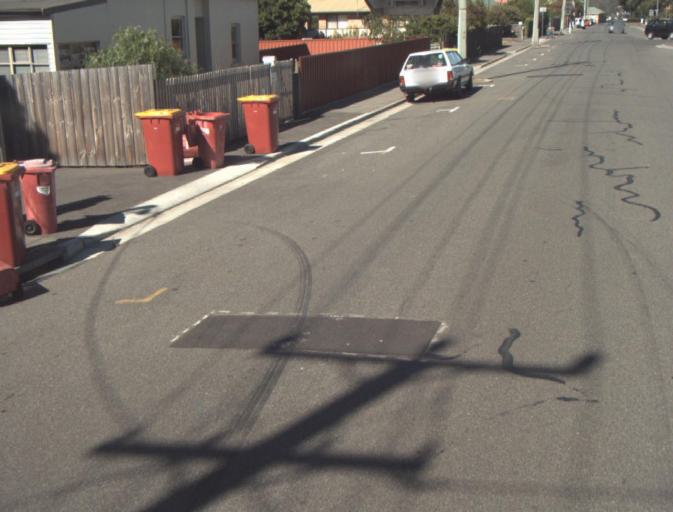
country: AU
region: Tasmania
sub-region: Launceston
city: Newnham
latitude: -41.4076
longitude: 147.1320
